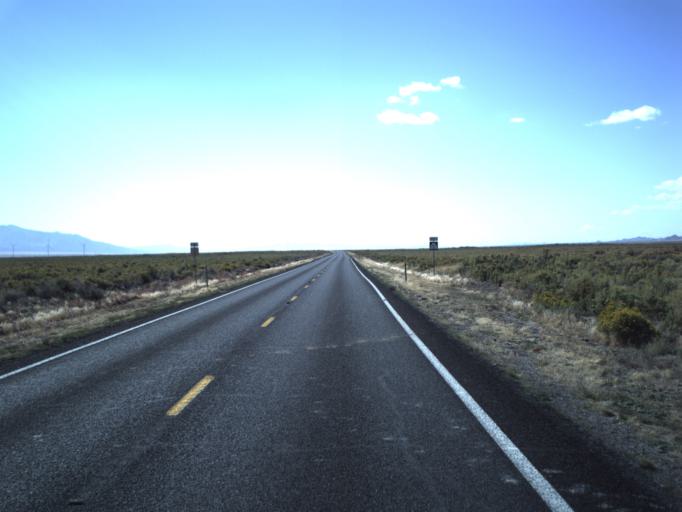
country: US
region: Utah
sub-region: Beaver County
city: Milford
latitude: 38.5658
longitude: -112.9905
